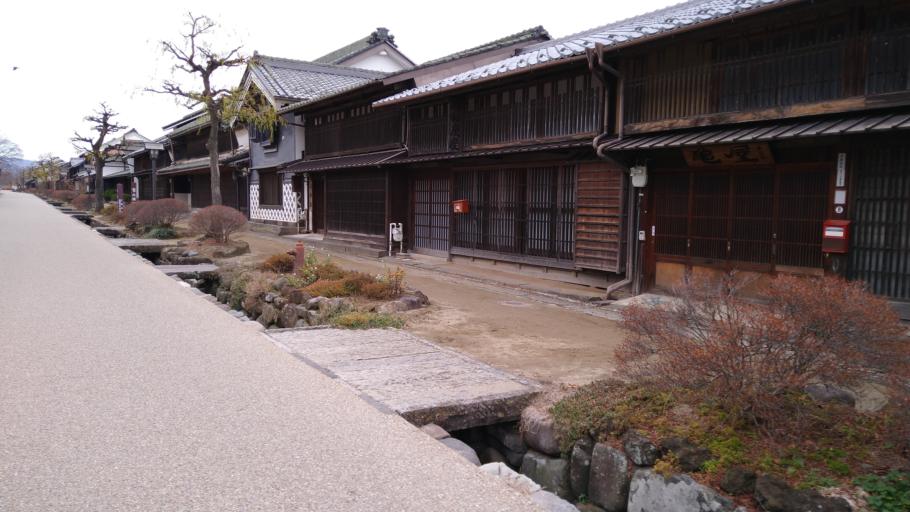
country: JP
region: Nagano
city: Ueda
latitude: 36.3617
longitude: 138.3135
